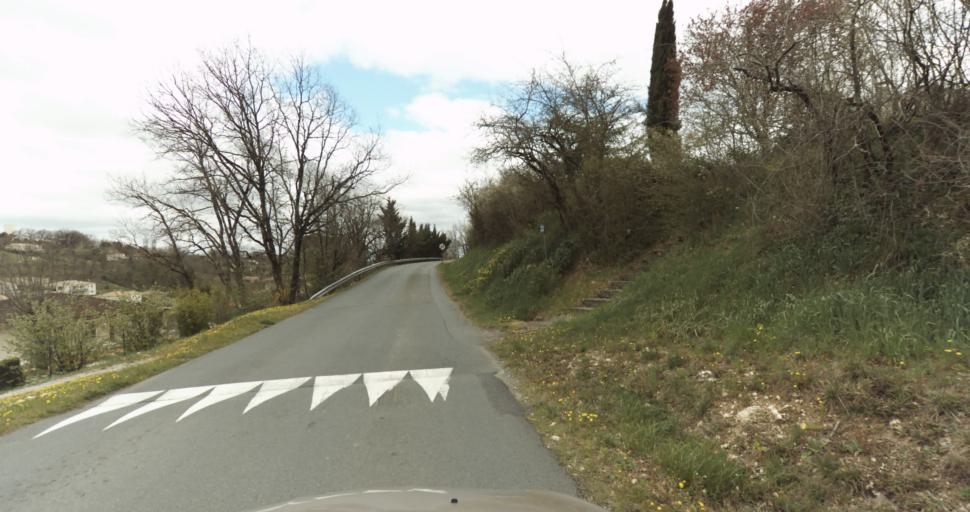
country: FR
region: Midi-Pyrenees
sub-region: Departement du Tarn
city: Puygouzon
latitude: 43.8990
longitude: 2.1734
